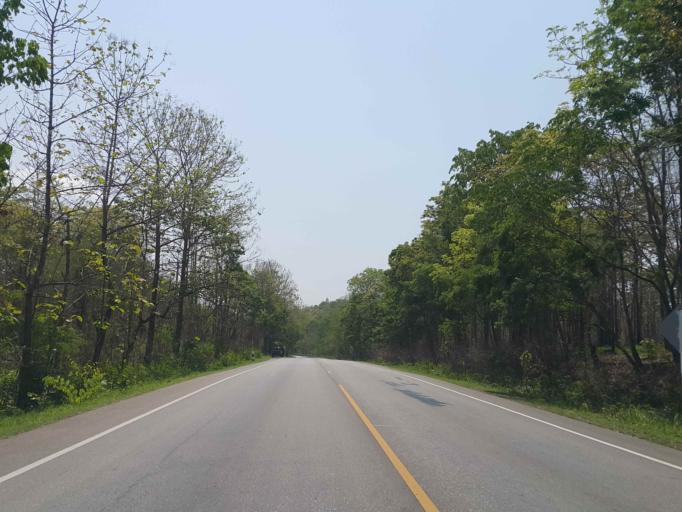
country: TH
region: Chiang Mai
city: Mae Taeng
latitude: 19.1036
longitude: 99.0611
